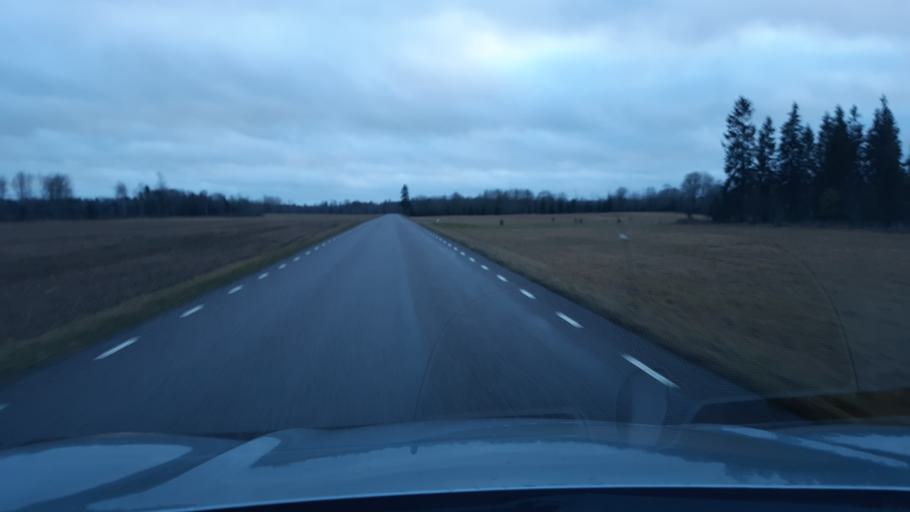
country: EE
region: Raplamaa
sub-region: Kohila vald
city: Kohila
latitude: 59.0952
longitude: 24.6735
